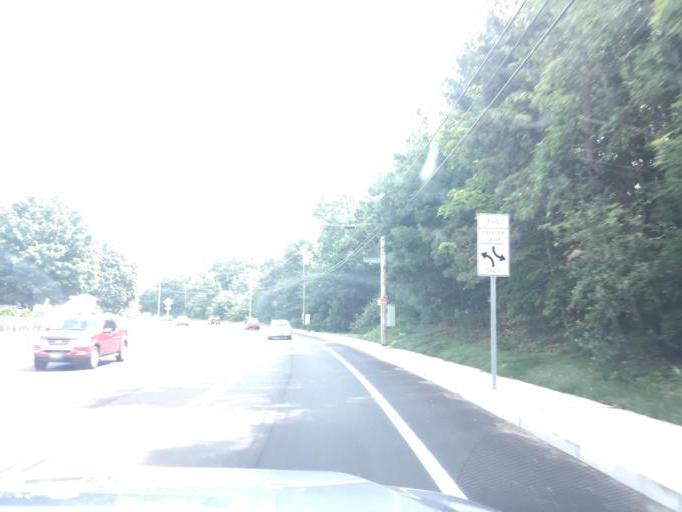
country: US
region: Rhode Island
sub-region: Kent County
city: West Warwick
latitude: 41.6682
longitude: -71.5513
